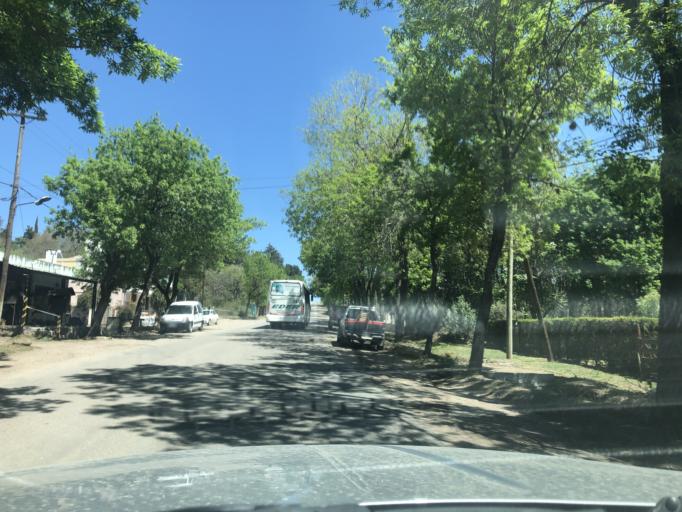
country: AR
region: Cordoba
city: La Granja
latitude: -31.0136
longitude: -64.2705
